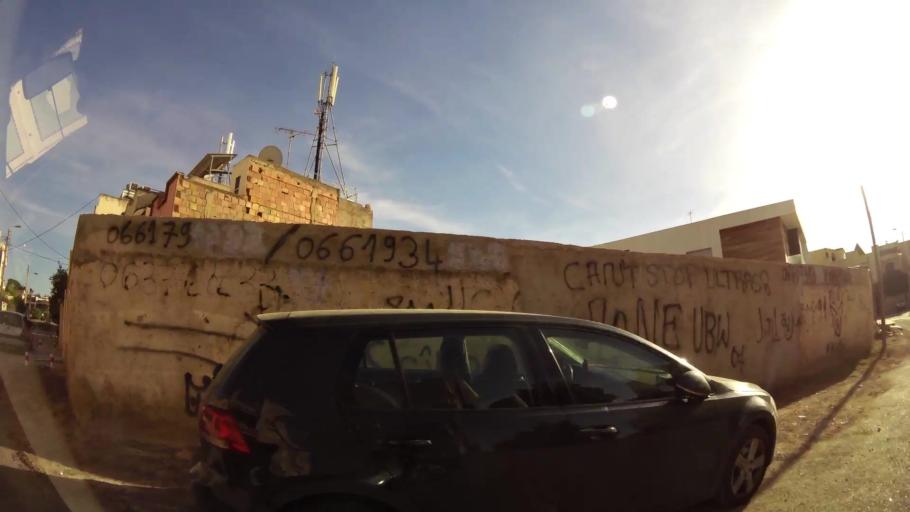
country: MA
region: Oriental
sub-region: Oujda-Angad
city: Oujda
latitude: 34.6694
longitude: -1.9023
